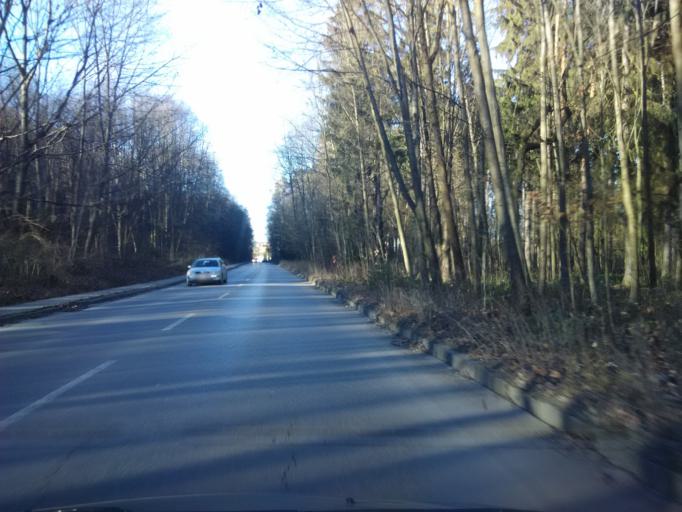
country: SK
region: Zilinsky
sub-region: Okres Zilina
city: Zilina
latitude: 49.2006
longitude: 18.7675
